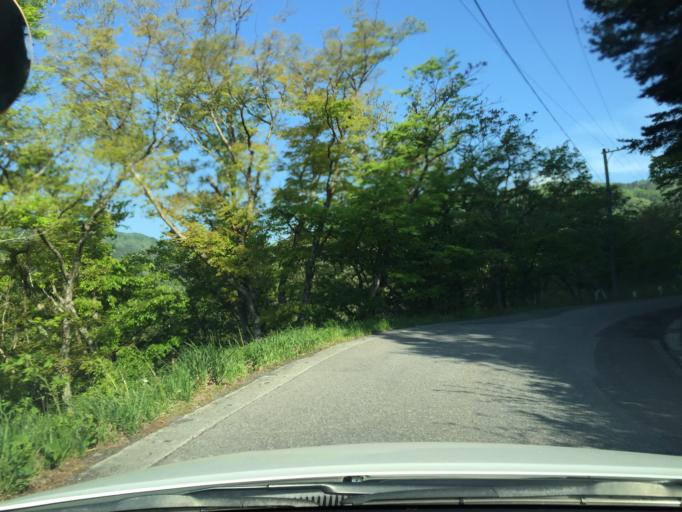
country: JP
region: Fukushima
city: Kitakata
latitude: 37.6676
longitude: 139.7445
